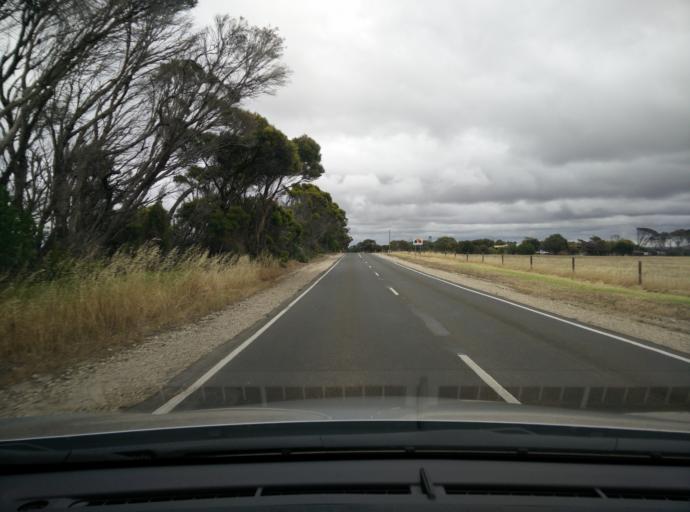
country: AU
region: South Australia
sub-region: Kangaroo Island
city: Kingscote
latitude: -35.6597
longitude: 137.6060
